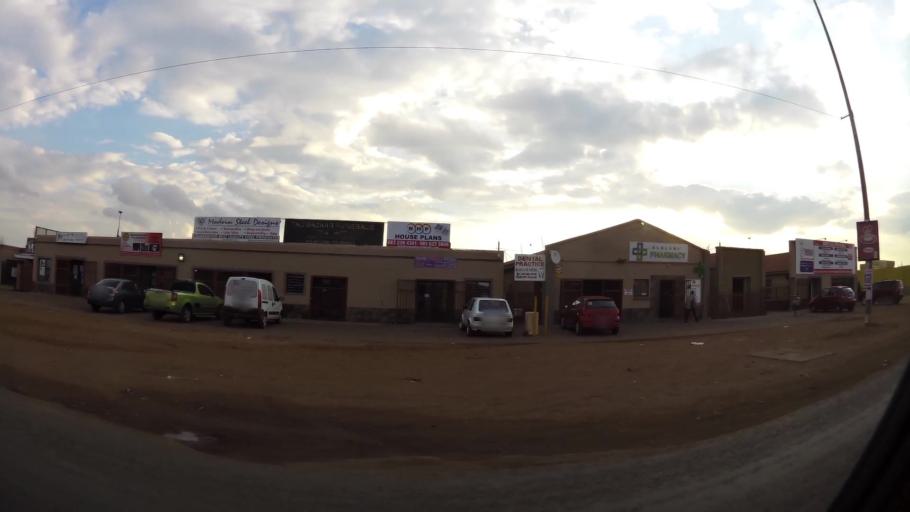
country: ZA
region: Gauteng
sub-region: City of Johannesburg Metropolitan Municipality
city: Orange Farm
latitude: -26.5910
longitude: 27.8470
